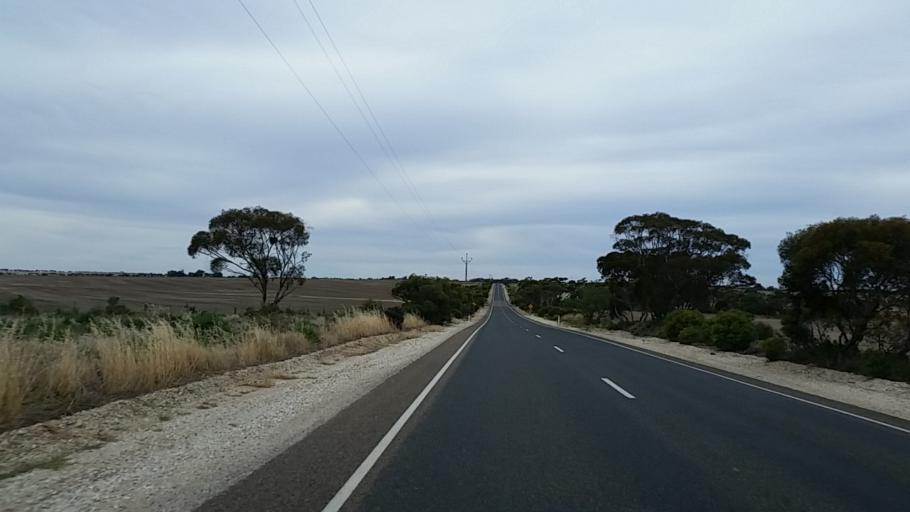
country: AU
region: South Australia
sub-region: Mid Murray
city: Mannum
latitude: -34.9145
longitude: 139.2672
